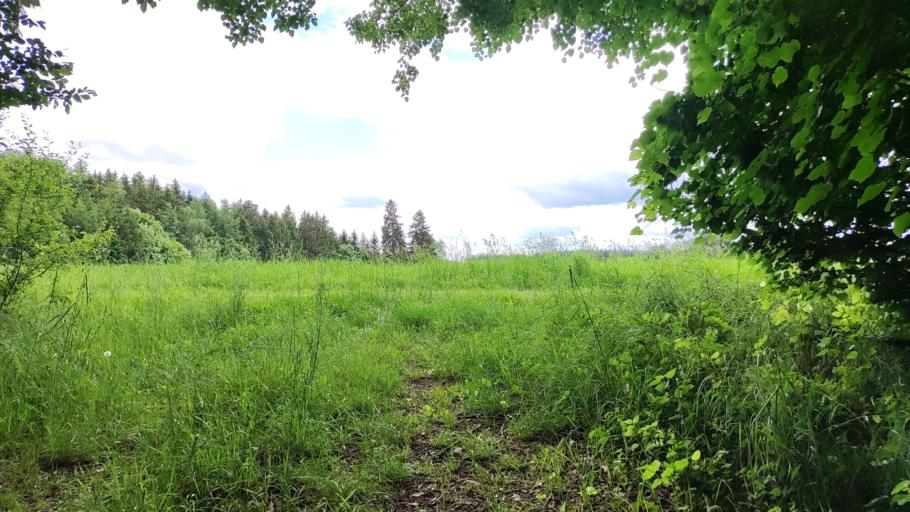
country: DE
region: Bavaria
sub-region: Swabia
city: Zusmarshausen
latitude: 48.3850
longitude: 10.5472
